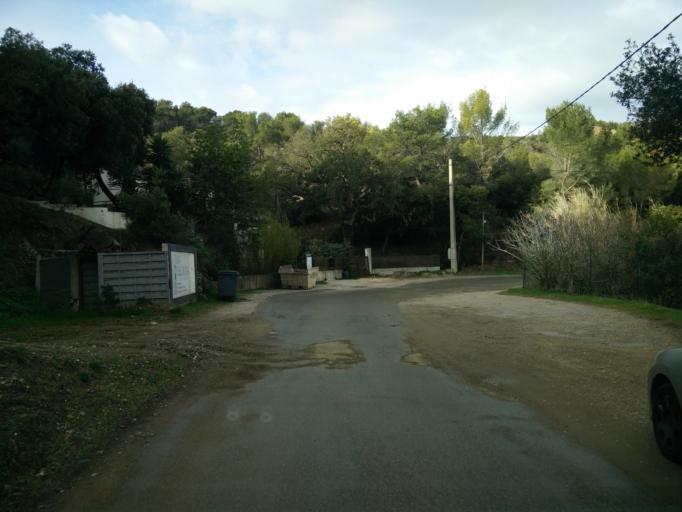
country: FR
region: Provence-Alpes-Cote d'Azur
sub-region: Departement du Var
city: Six-Fours-les-Plages
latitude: 43.0641
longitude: 5.8286
